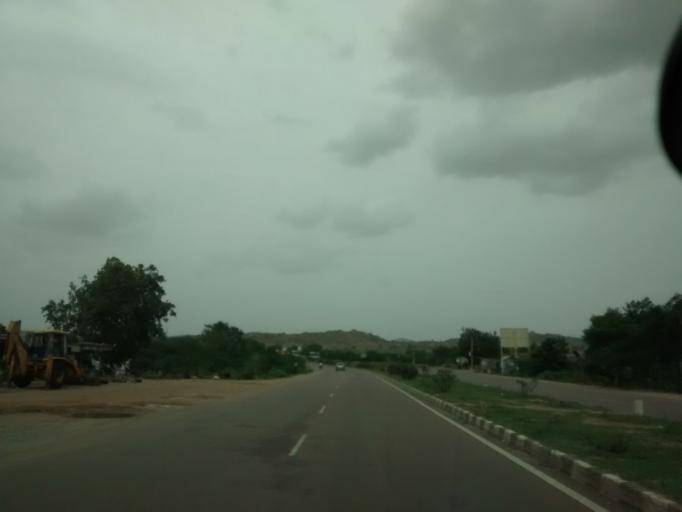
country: IN
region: Andhra Pradesh
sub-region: Kurnool
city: Ramapuram
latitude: 15.1709
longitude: 77.6825
